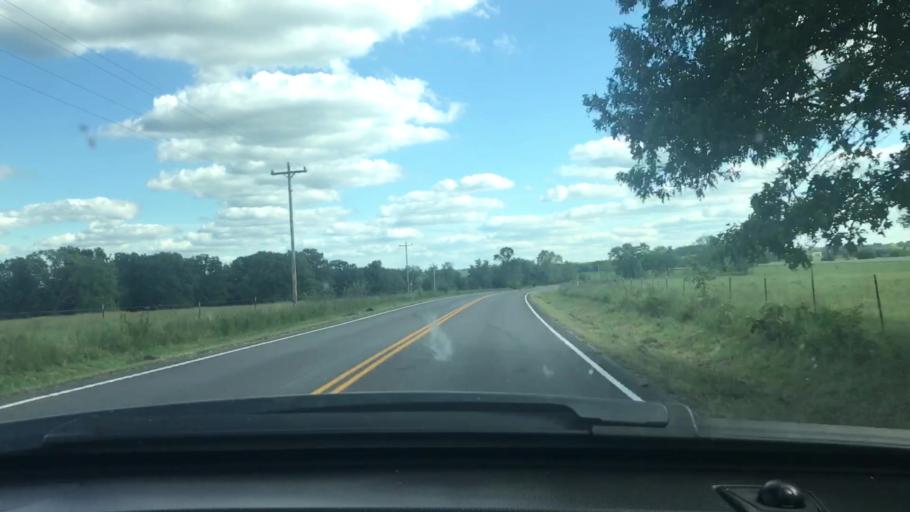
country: US
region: Missouri
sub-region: Wright County
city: Mountain Grove
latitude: 37.2968
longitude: -92.3101
